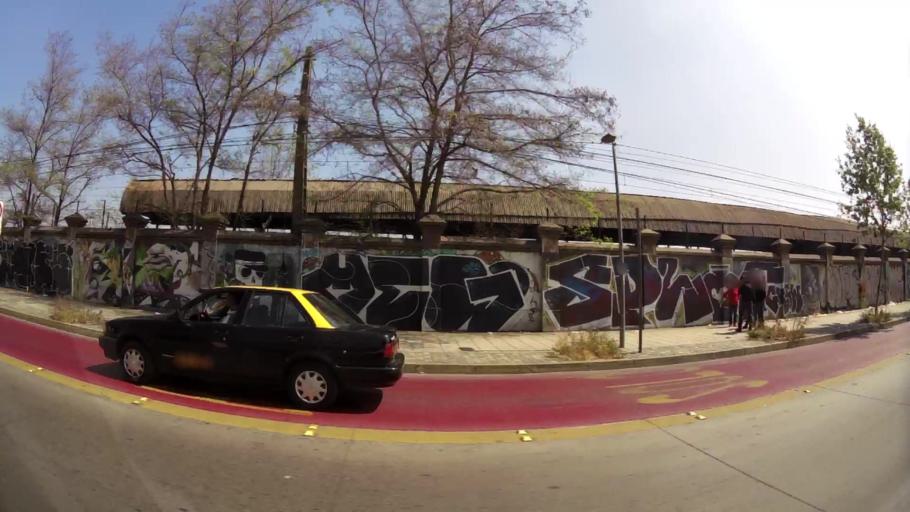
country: CL
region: Santiago Metropolitan
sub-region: Provincia de Santiago
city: Santiago
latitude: -33.4569
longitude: -70.6783
